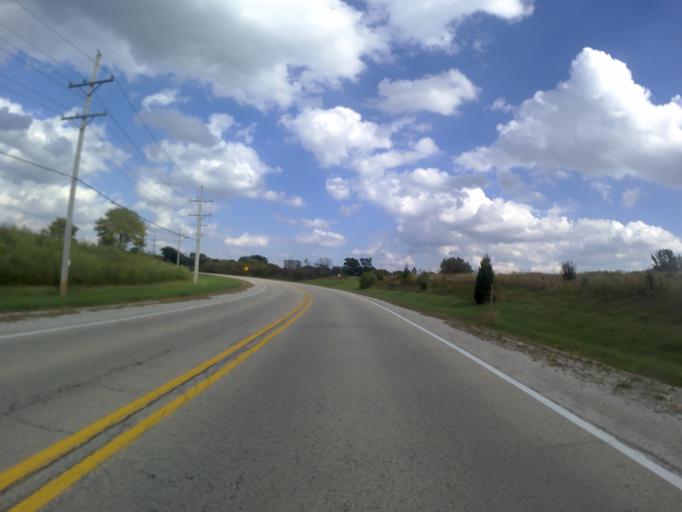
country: US
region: Illinois
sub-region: DuPage County
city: Lisle
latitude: 41.8257
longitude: -88.0954
